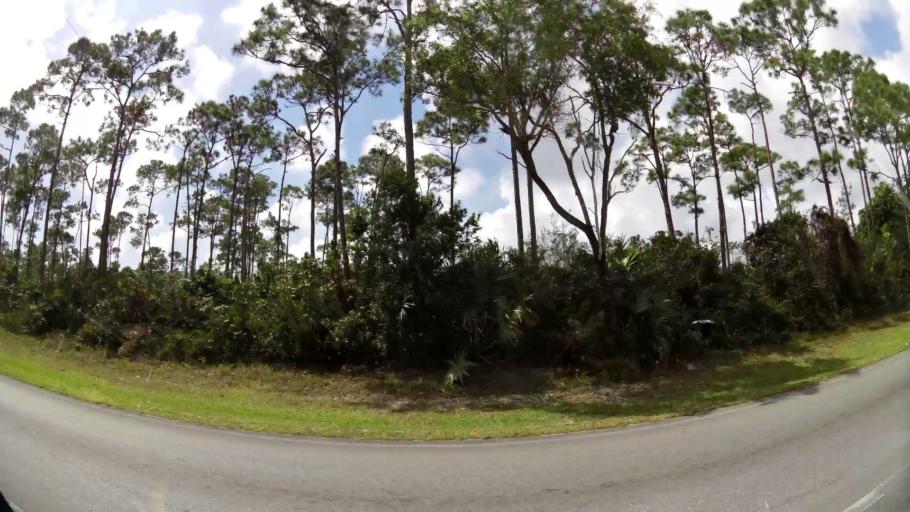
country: BS
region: Freeport
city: Lucaya
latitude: 26.5362
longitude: -78.6611
